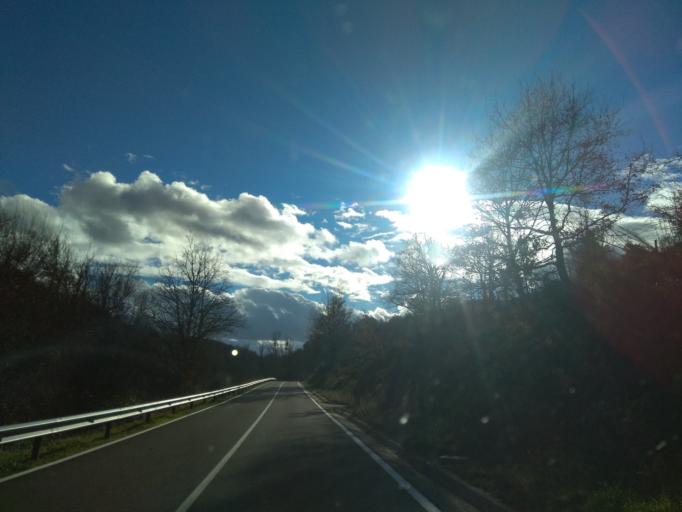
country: ES
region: Cantabria
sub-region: Provincia de Cantabria
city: San Martin de Elines
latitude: 42.8889
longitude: -3.9100
